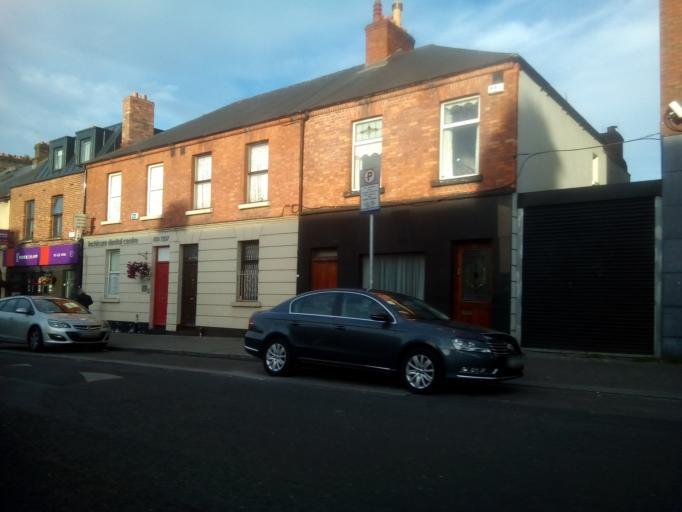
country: IE
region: Leinster
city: Crumlin
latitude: 53.3368
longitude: -6.3223
